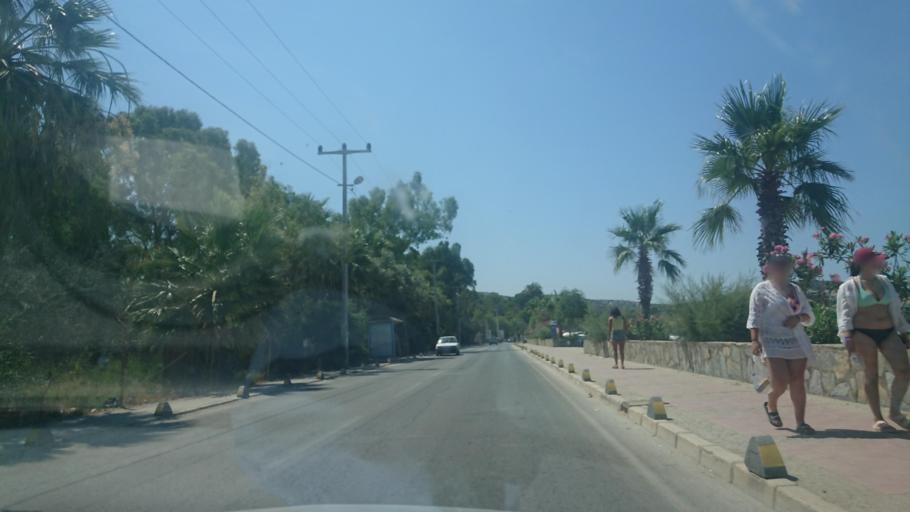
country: TR
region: Aydin
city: Kusadasi
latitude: 37.9032
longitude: 27.2725
